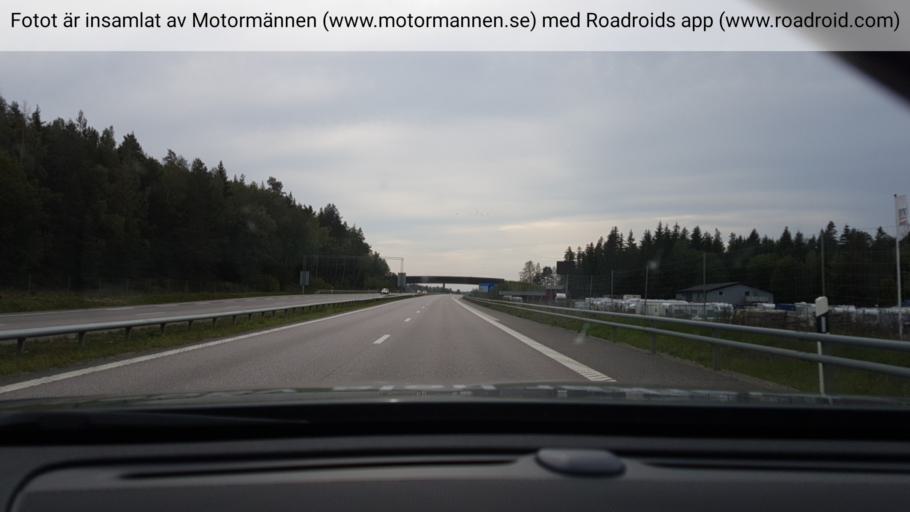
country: SE
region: Stockholm
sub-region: Nynashamns Kommun
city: Osmo
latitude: 58.9659
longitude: 17.9080
